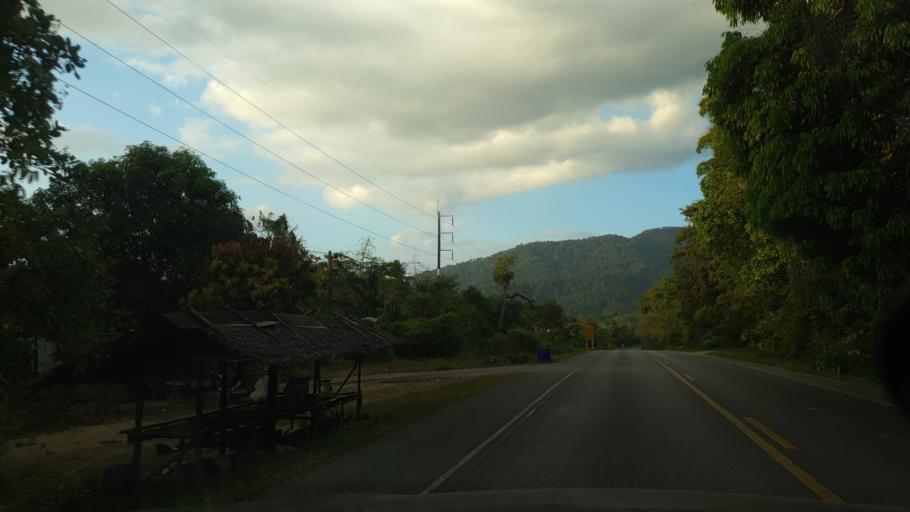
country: TH
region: Phangnga
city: Takua Pa
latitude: 8.9143
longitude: 98.4087
